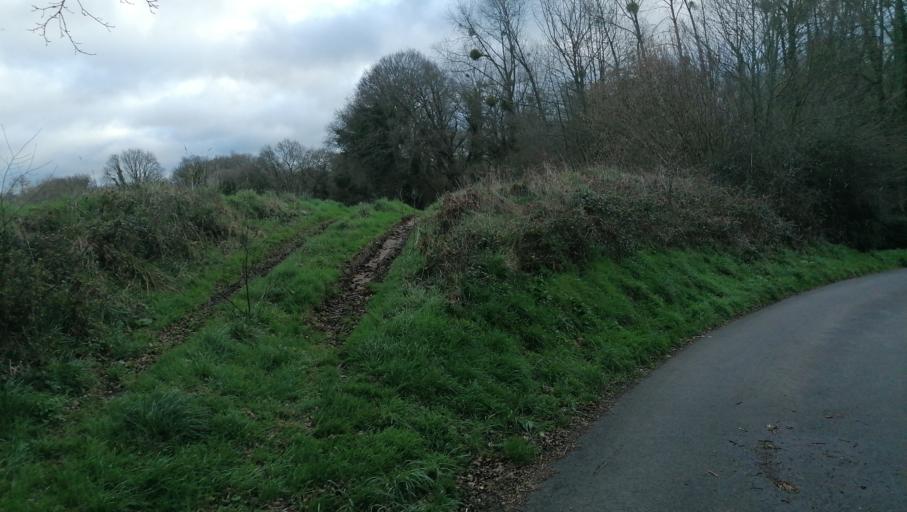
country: FR
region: Brittany
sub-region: Departement des Cotes-d'Armor
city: Pommerit-le-Vicomte
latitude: 48.6489
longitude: -3.0796
